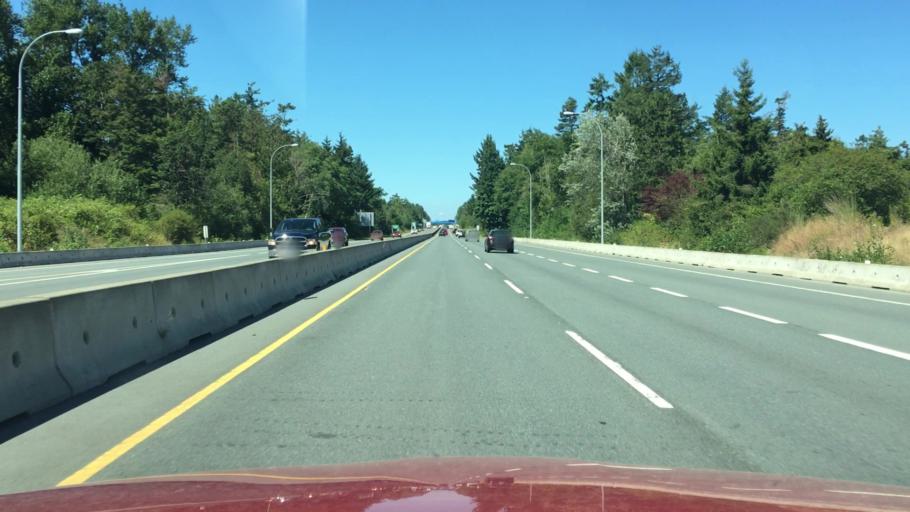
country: CA
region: British Columbia
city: North Saanich
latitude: 48.6328
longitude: -123.4110
